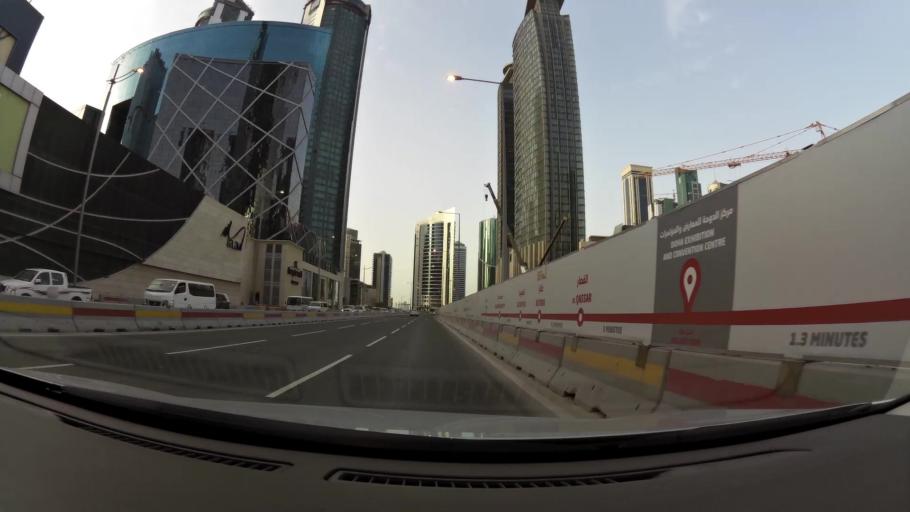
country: QA
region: Baladiyat ad Dawhah
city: Doha
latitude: 25.3225
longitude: 51.5275
